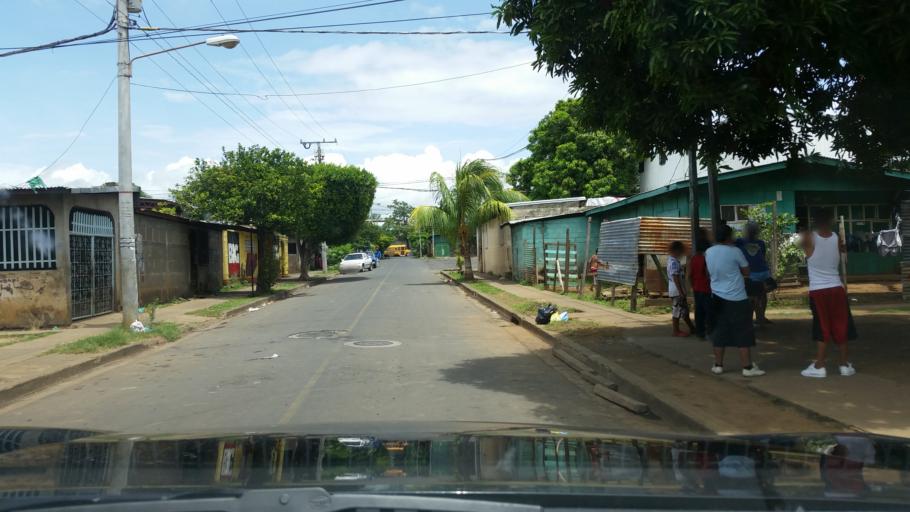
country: NI
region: Managua
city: Managua
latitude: 12.1252
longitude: -86.2480
